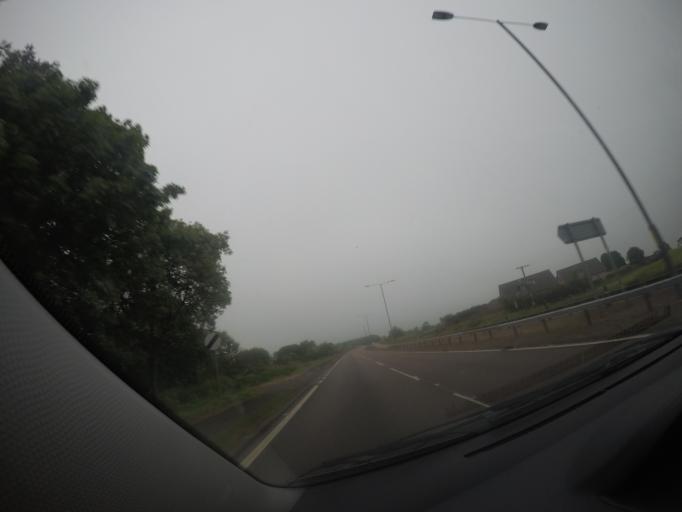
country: GB
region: Scotland
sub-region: Dundee City
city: Dundee
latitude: 56.5240
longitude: -2.9448
